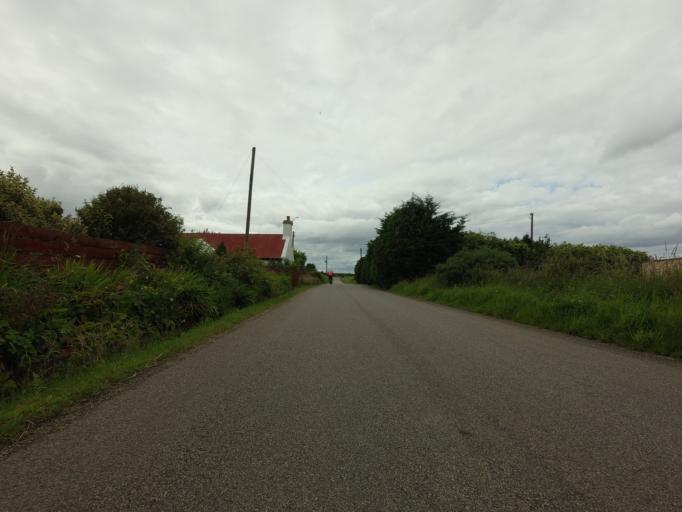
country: GB
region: Scotland
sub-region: Moray
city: Forres
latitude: 57.6035
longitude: -3.7265
